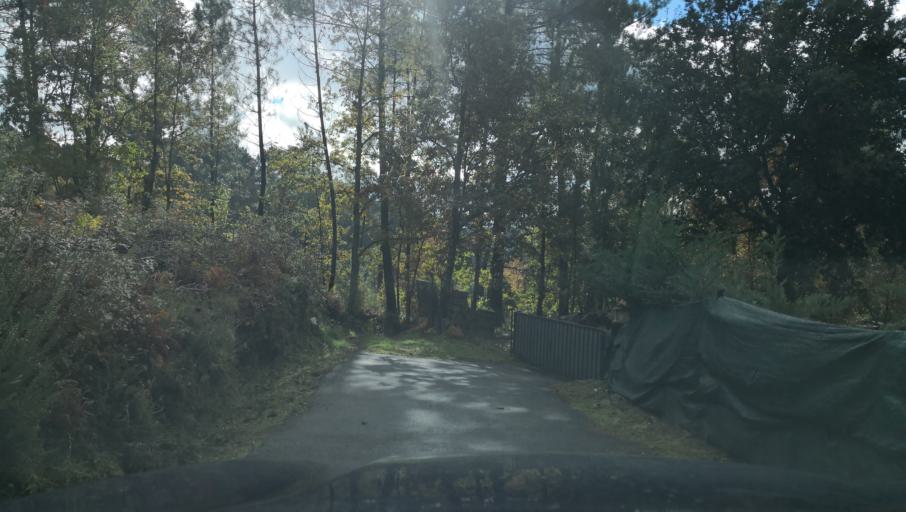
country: PT
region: Vila Real
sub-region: Vila Real
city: Vila Real
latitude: 41.3203
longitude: -7.7555
